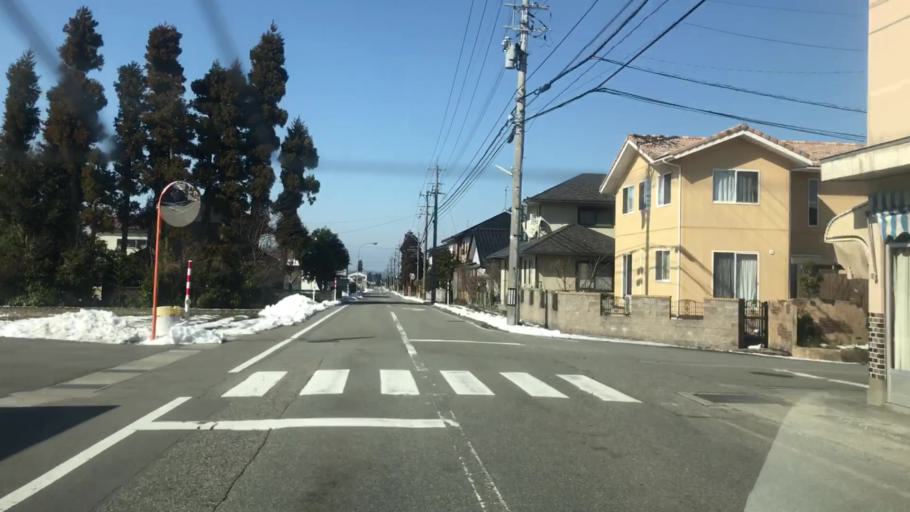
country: JP
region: Toyama
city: Toyama-shi
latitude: 36.6239
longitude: 137.2801
